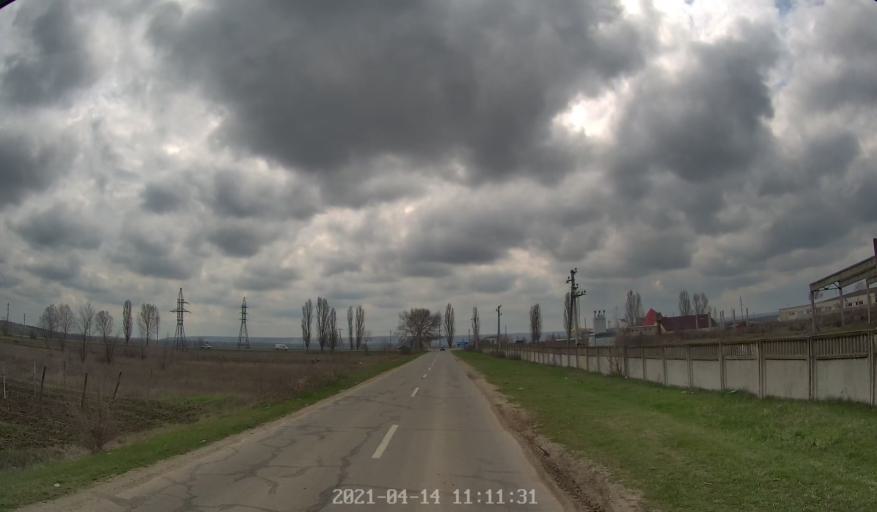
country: MD
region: Criuleni
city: Criuleni
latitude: 47.1542
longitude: 29.1522
